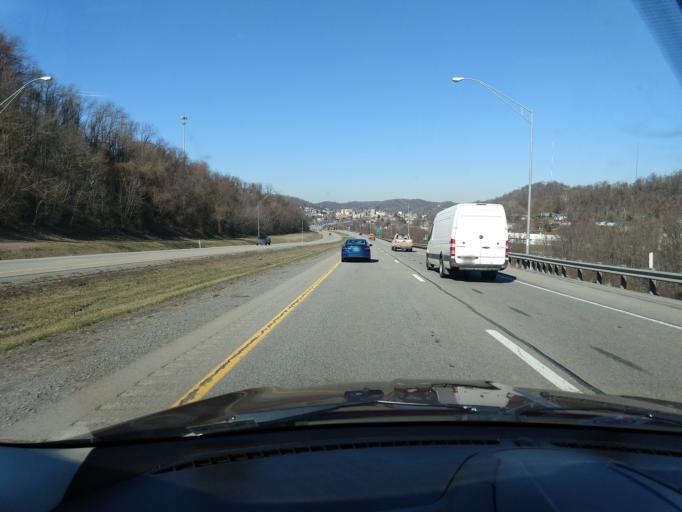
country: US
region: West Virginia
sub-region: Harrison County
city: Despard
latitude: 39.2771
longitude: -80.3086
